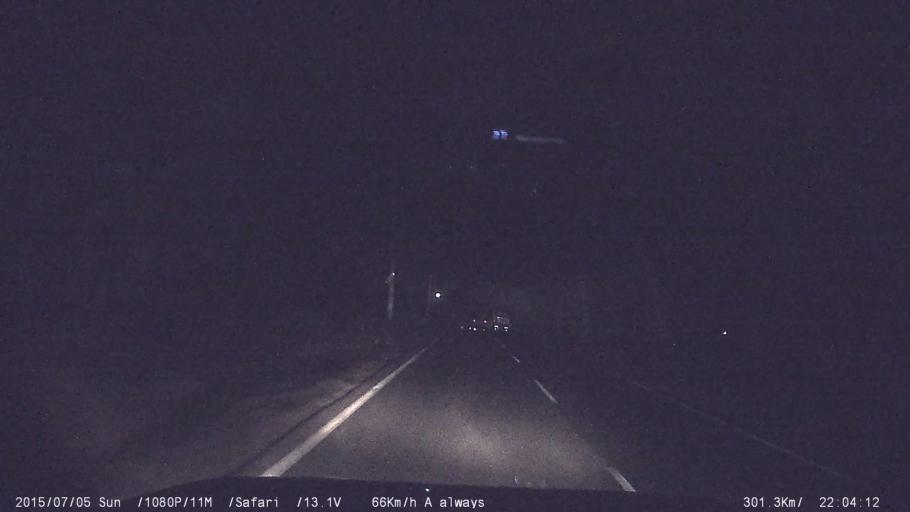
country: IN
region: Kerala
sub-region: Palakkad district
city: Mannarakkat
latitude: 10.9241
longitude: 76.5241
